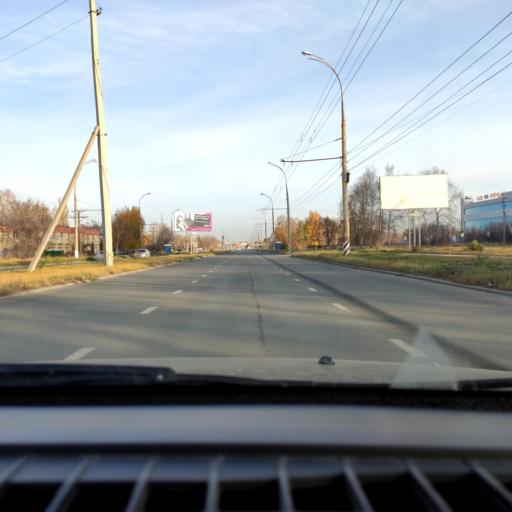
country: RU
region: Samara
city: Tol'yatti
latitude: 53.5414
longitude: 49.3006
